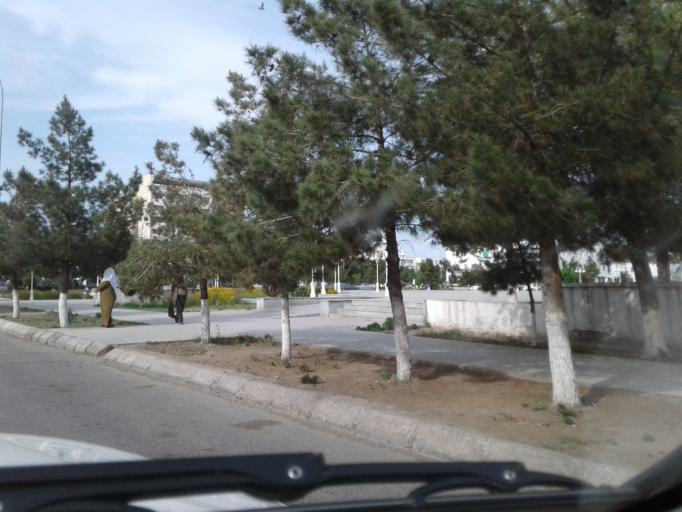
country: TM
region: Mary
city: Mary
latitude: 37.5941
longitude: 61.8347
